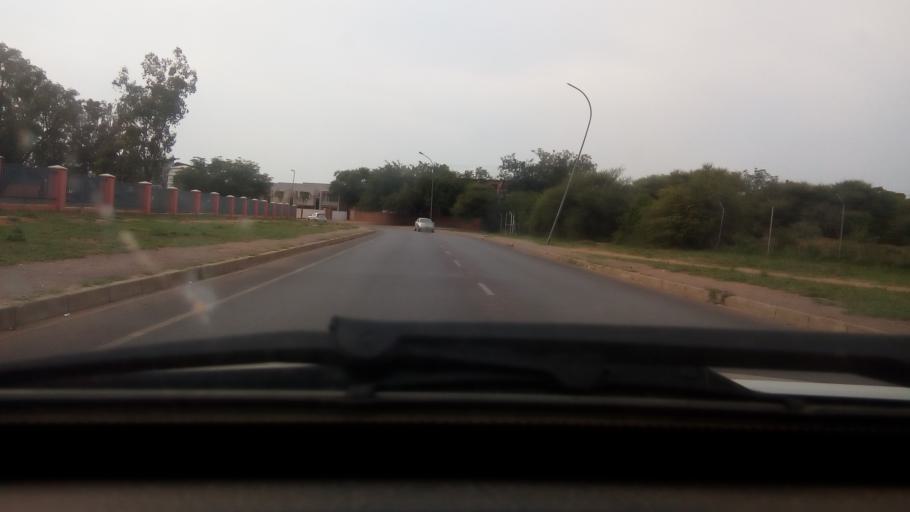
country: BW
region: South East
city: Gaborone
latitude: -24.6658
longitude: 25.9343
